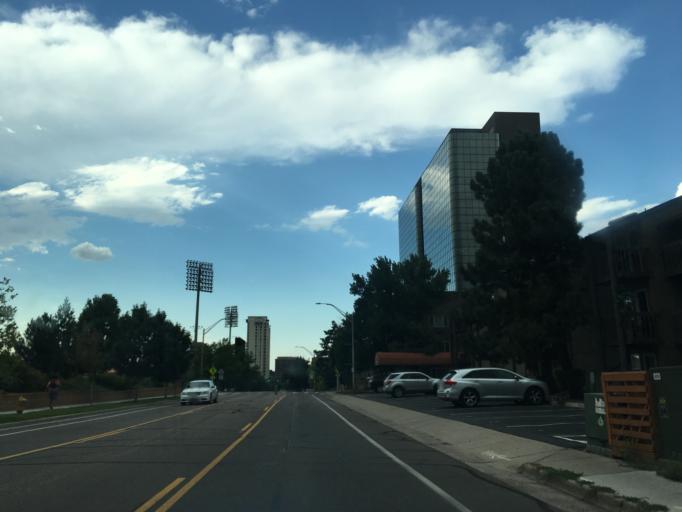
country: US
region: Colorado
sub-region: Arapahoe County
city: Glendale
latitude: 39.6975
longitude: -104.9340
